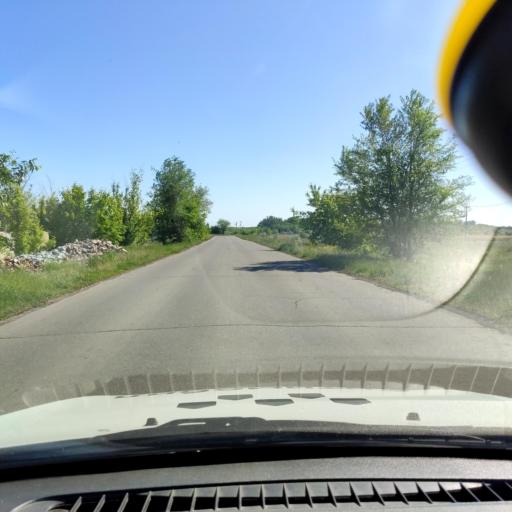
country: RU
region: Samara
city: Tol'yatti
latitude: 53.6473
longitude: 49.3198
